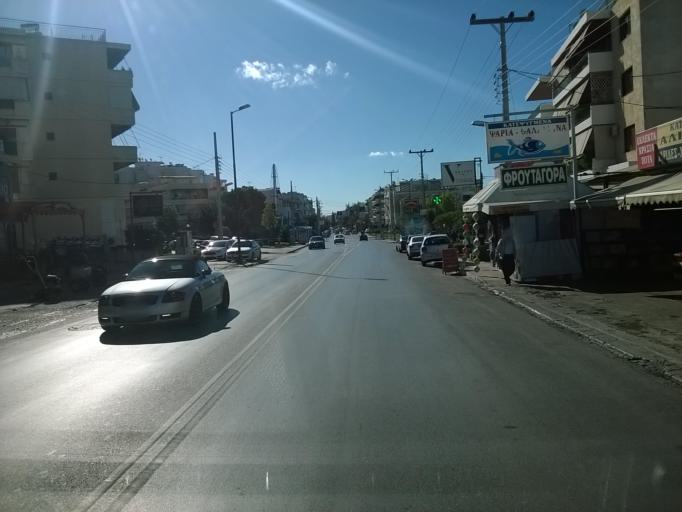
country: GR
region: Attica
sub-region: Nomarchia Athinas
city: Argyroupoli
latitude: 37.8900
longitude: 23.7611
